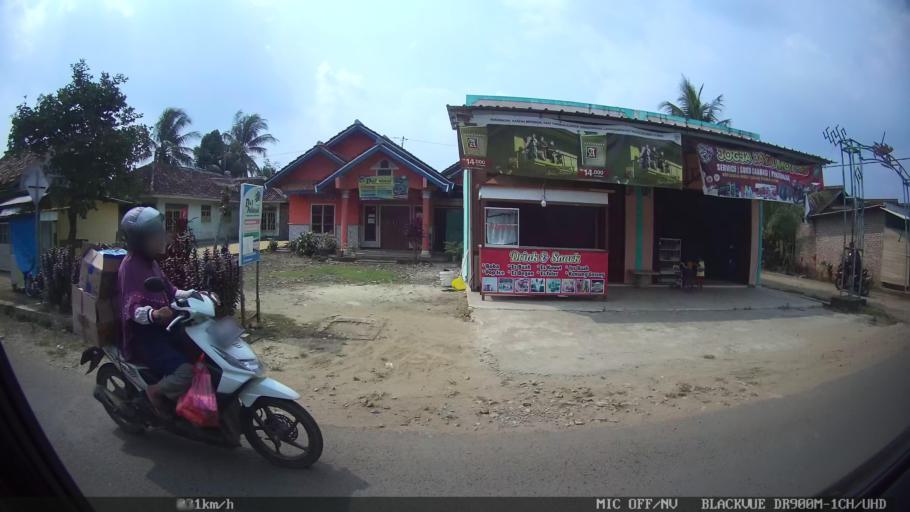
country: ID
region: Lampung
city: Gadingrejo
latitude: -5.3503
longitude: 105.0242
